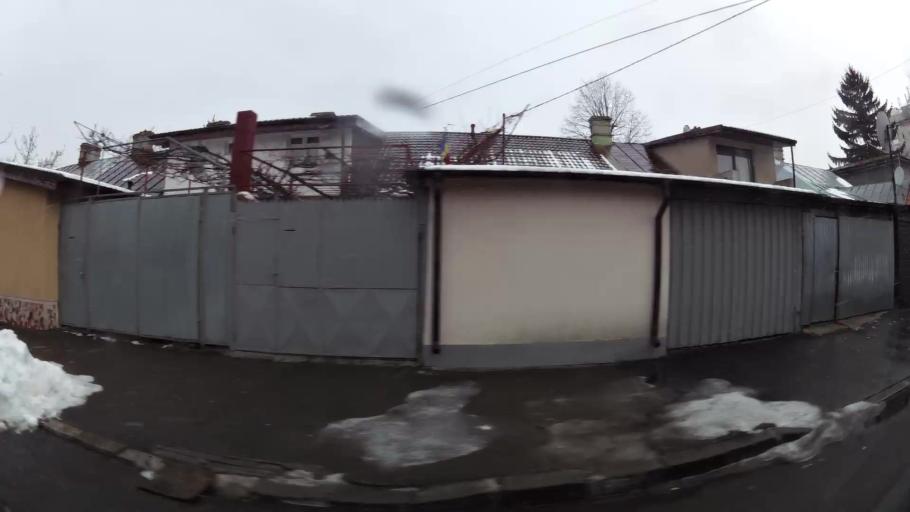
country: RO
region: Ilfov
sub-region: Comuna Mogosoaia
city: Mogosoaia
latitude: 44.4980
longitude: 26.0384
